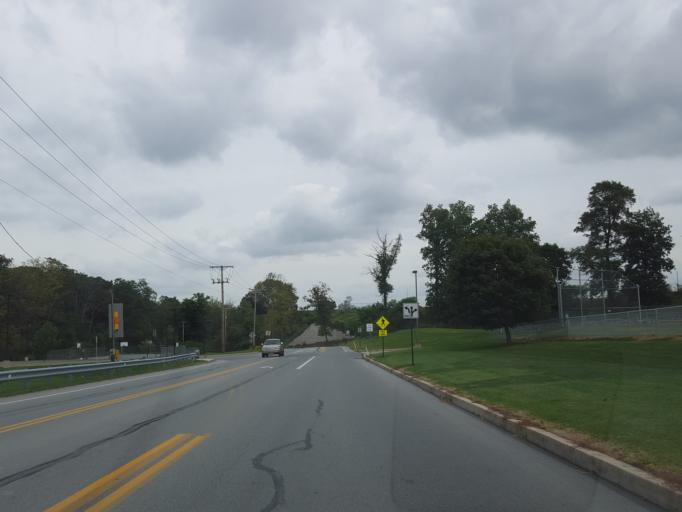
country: US
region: Pennsylvania
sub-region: York County
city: Red Lion
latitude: 39.8924
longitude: -76.6063
